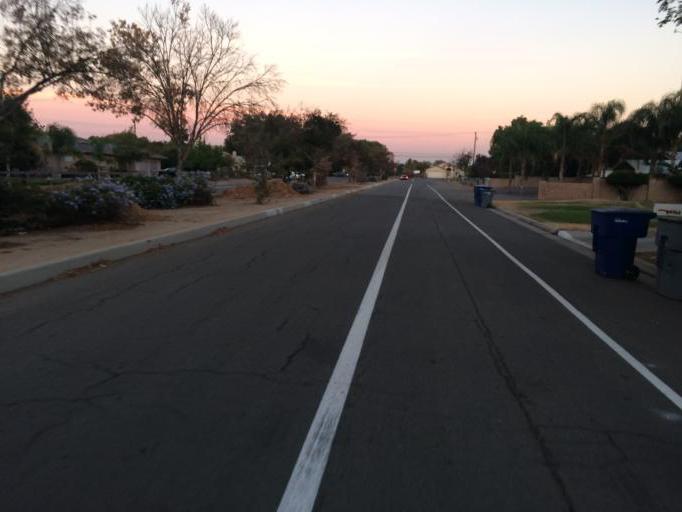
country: US
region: California
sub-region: Fresno County
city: Sunnyside
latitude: 36.7468
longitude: -119.7294
